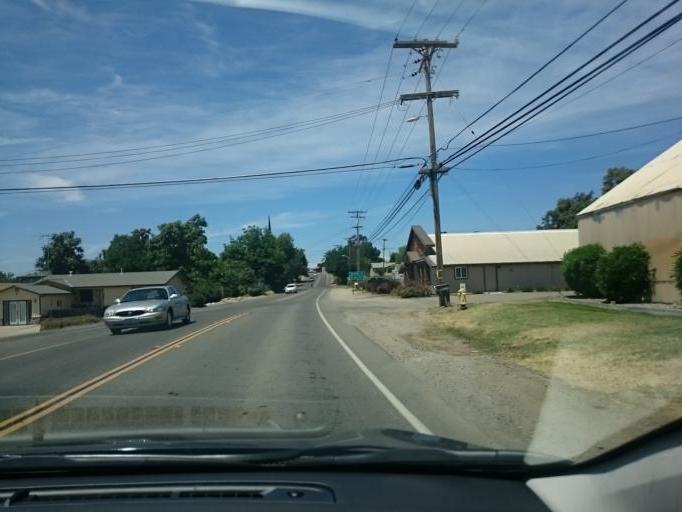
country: US
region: California
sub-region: Stanislaus County
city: Waterford
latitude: 37.6394
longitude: -120.7541
